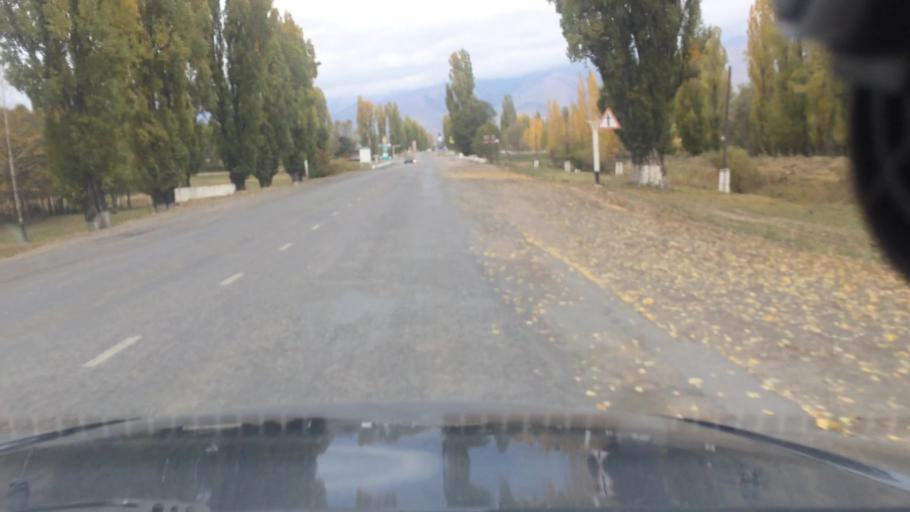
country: KG
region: Ysyk-Koel
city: Tyup
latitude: 42.7371
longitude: 78.3483
